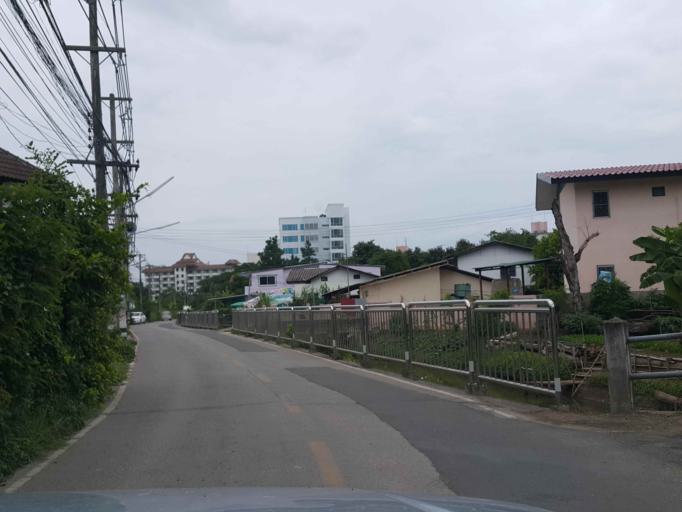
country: TH
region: Chiang Mai
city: Chiang Mai
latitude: 18.7628
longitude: 99.0136
